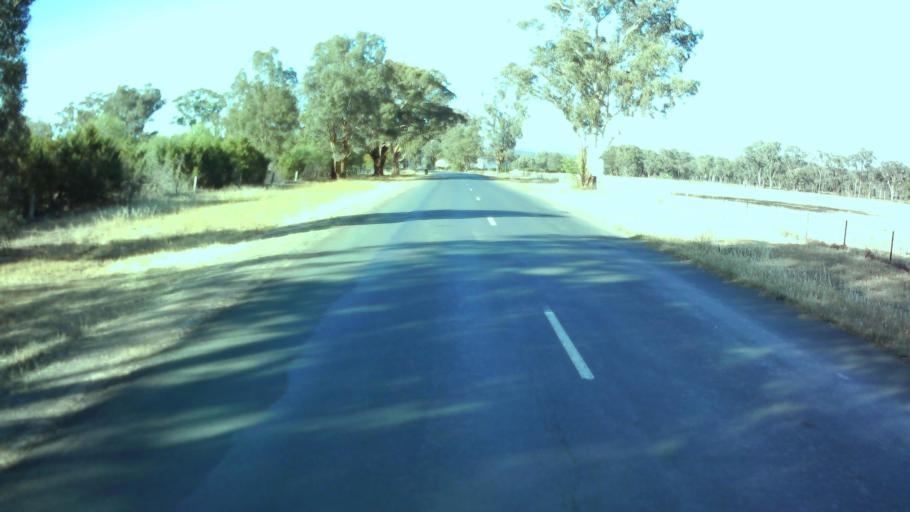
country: AU
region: New South Wales
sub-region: Weddin
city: Grenfell
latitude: -33.9022
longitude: 148.1509
